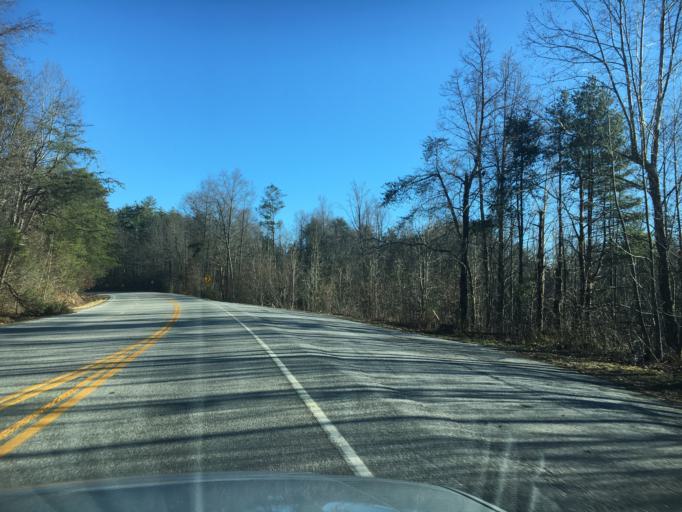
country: US
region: Georgia
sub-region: White County
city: Cleveland
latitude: 34.6876
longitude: -83.9077
